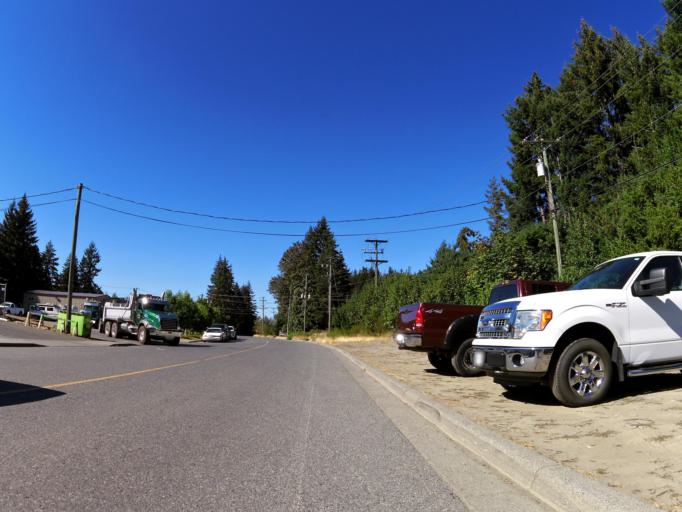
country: CA
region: British Columbia
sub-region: Cowichan Valley Regional District
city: Ladysmith
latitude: 49.0043
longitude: -123.8317
